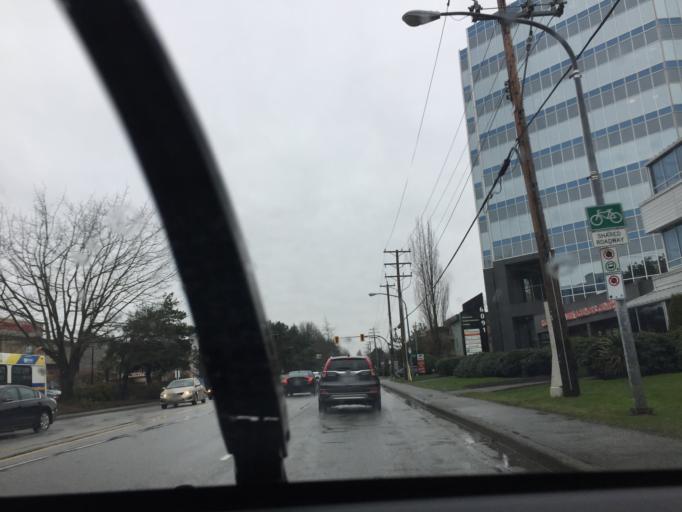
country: CA
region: British Columbia
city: Richmond
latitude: 49.1699
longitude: -123.1478
